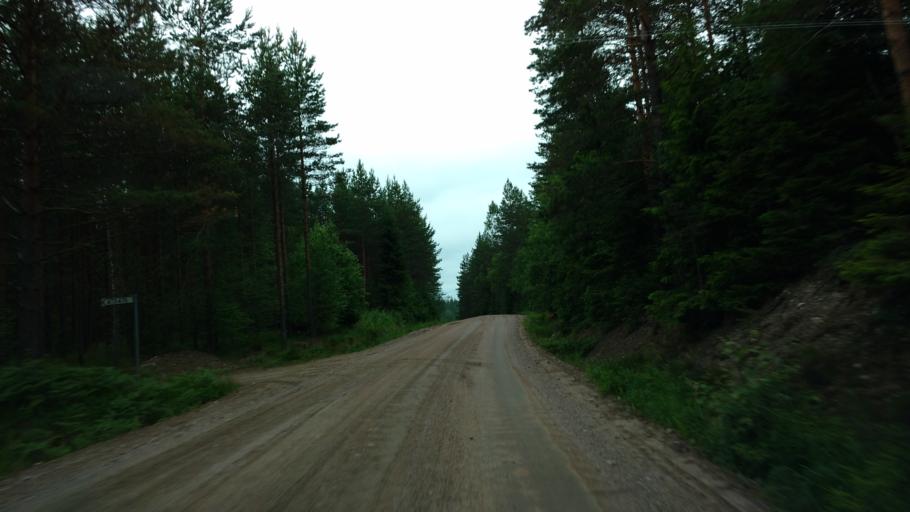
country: FI
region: Varsinais-Suomi
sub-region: Salo
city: Kiikala
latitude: 60.4879
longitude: 23.6595
